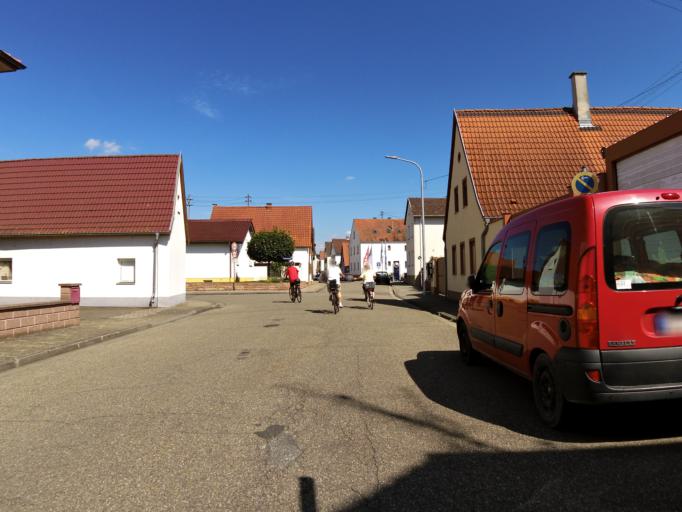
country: DE
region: Rheinland-Pfalz
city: Hanhofen
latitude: 49.3149
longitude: 8.3432
